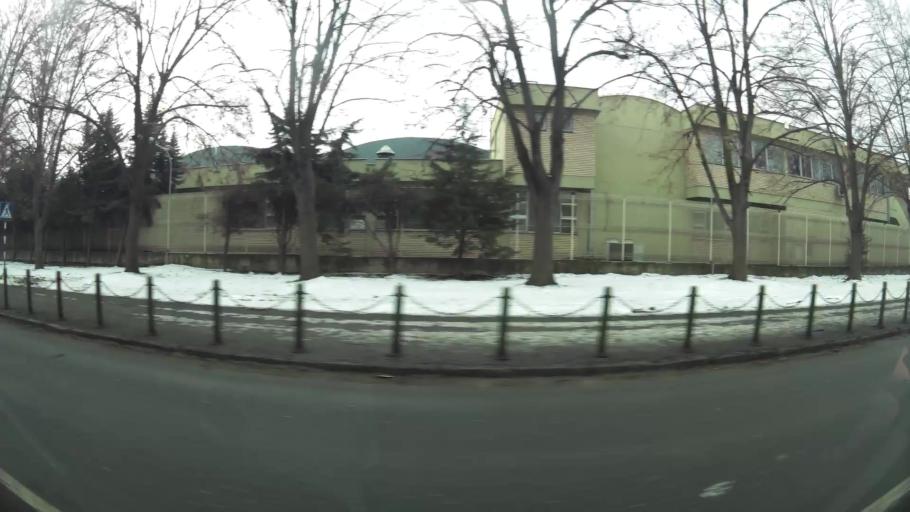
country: MK
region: Cair
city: Cair
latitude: 41.9995
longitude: 21.4674
